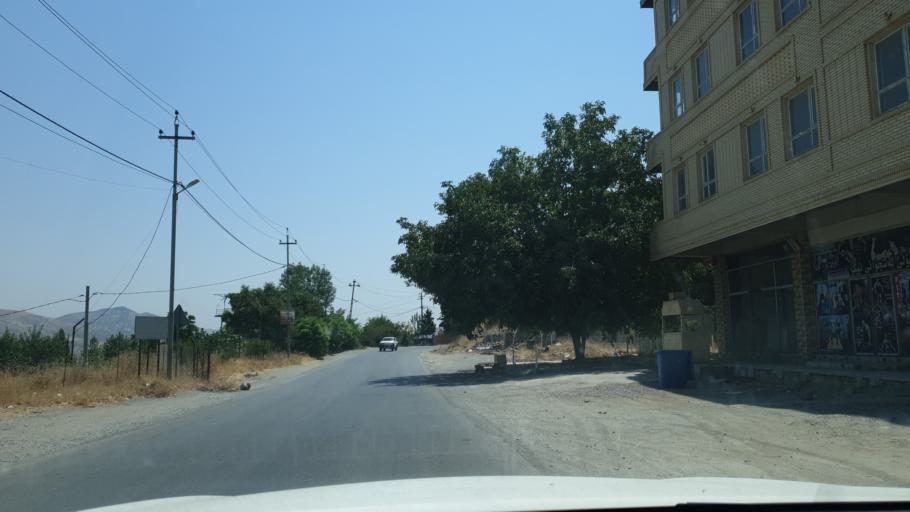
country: IQ
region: Arbil
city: Nahiyat Hiran
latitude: 36.2832
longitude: 44.4910
